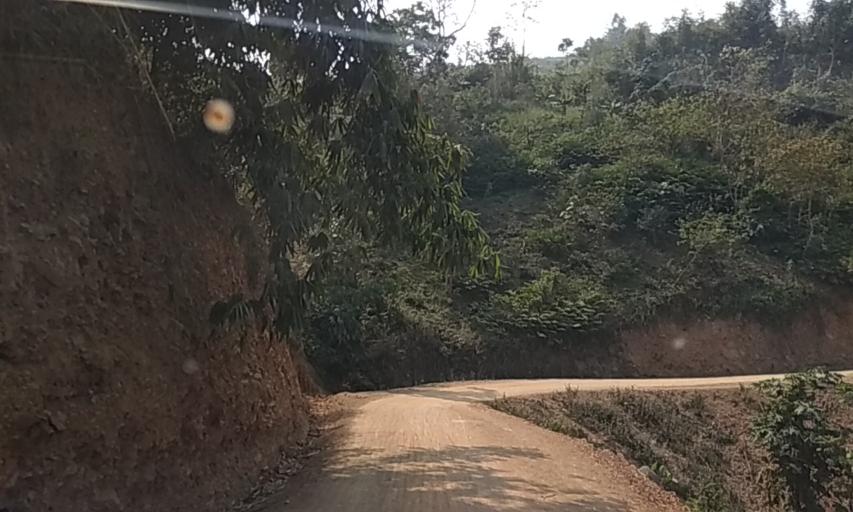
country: LA
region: Phongsali
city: Phongsali
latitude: 21.4765
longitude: 102.4400
